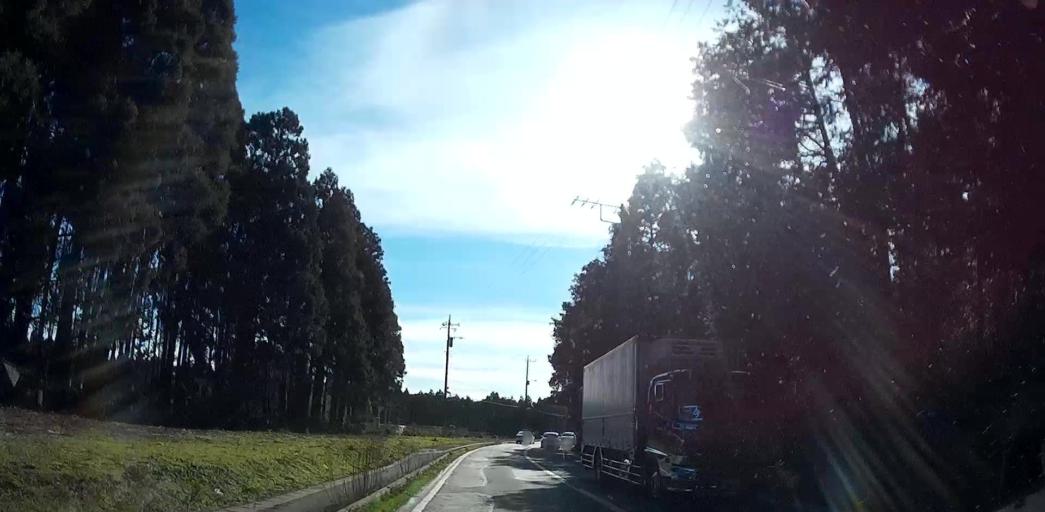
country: JP
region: Chiba
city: Yokaichiba
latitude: 35.7579
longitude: 140.4564
